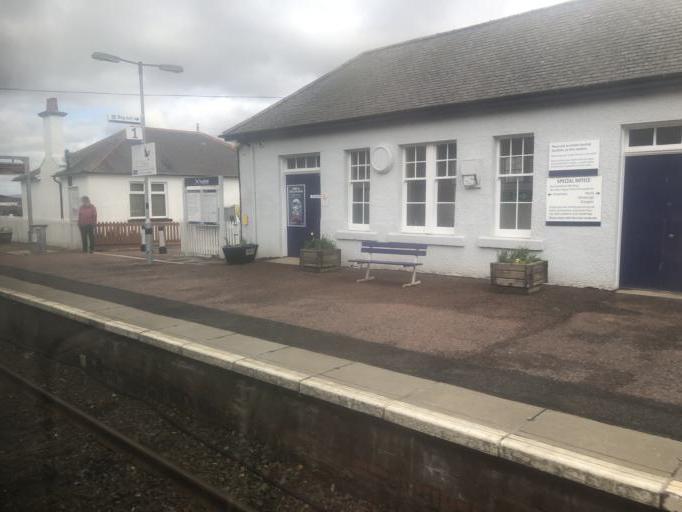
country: GB
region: Scotland
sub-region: Highland
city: Kingussie
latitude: 56.9351
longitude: -4.2462
